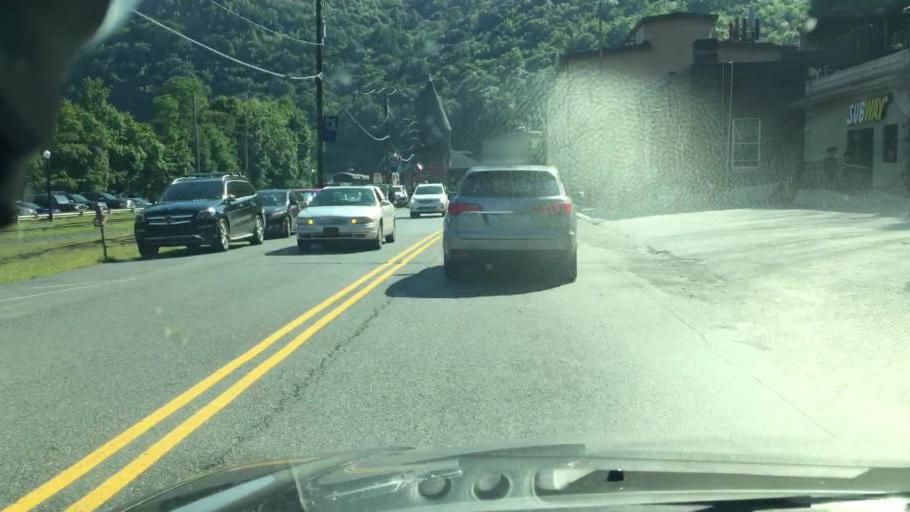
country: US
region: Pennsylvania
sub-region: Carbon County
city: Jim Thorpe
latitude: 40.8646
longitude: -75.7365
